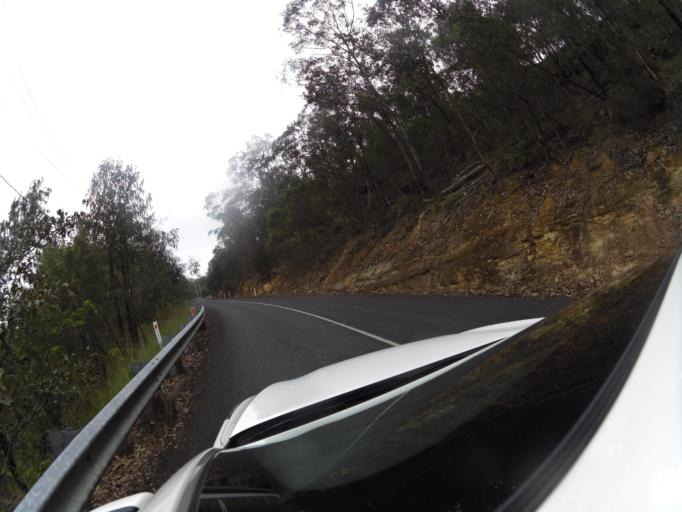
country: AU
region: New South Wales
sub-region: Hawkesbury
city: Pitt Town
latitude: -33.4338
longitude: 150.9237
